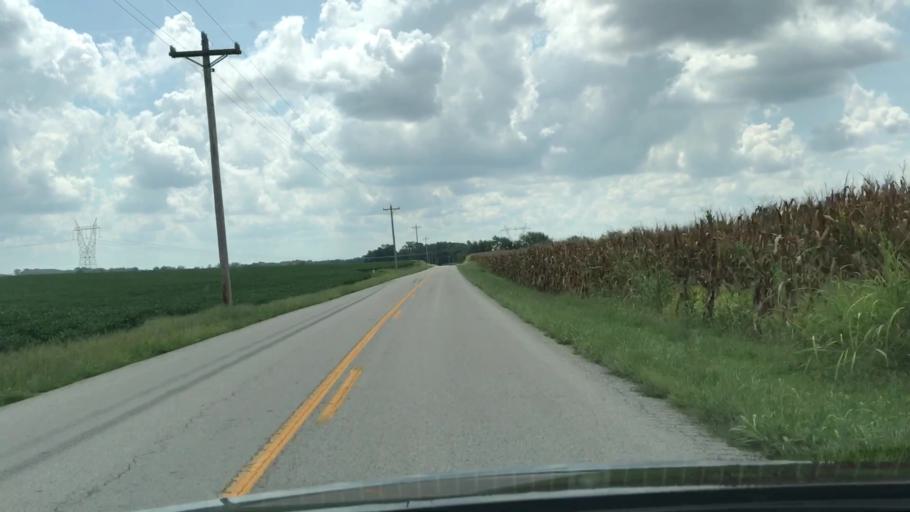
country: US
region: Kentucky
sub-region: Todd County
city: Elkton
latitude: 36.7778
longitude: -87.1199
